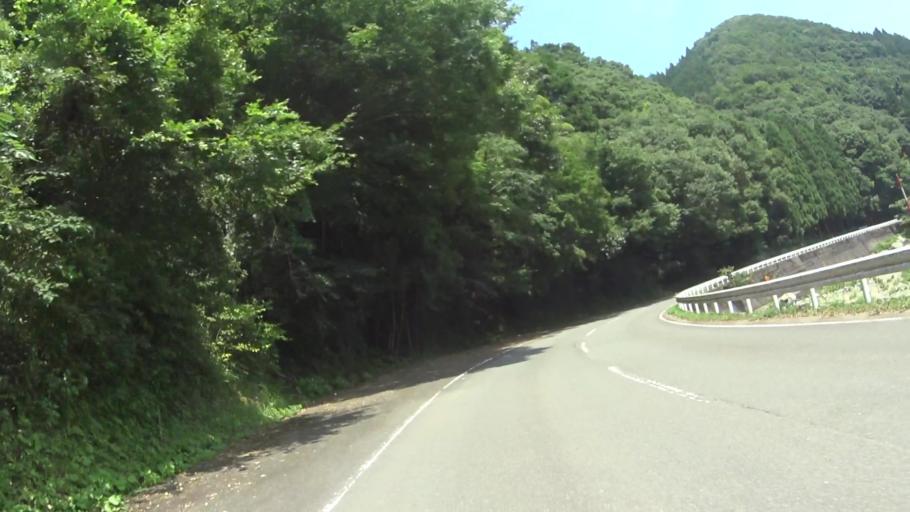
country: JP
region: Kyoto
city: Maizuru
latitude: 35.3081
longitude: 135.4310
